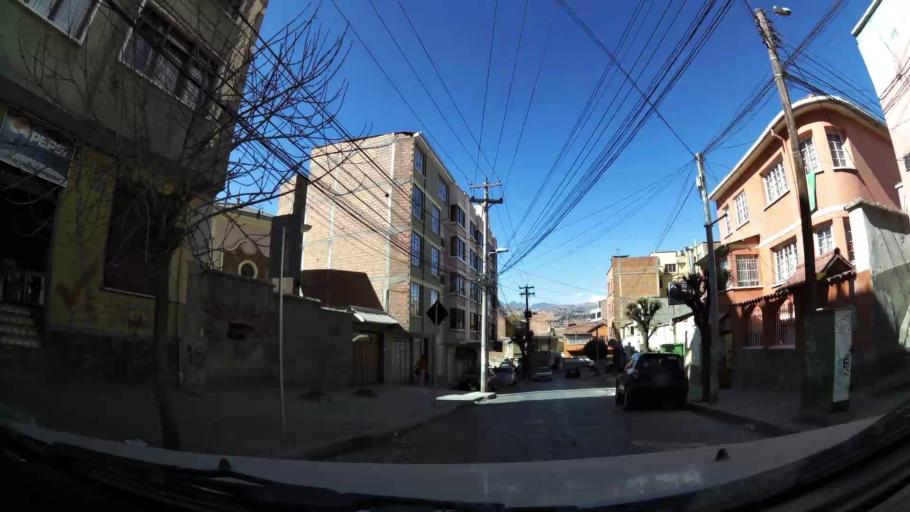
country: BO
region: La Paz
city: La Paz
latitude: -16.5088
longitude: -68.1352
